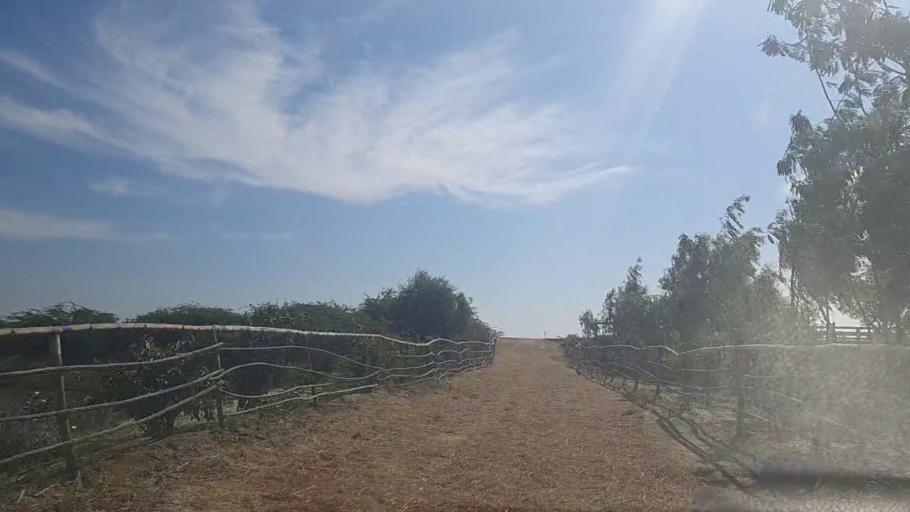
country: PK
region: Sindh
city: Mirpur Batoro
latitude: 24.6537
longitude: 68.2030
